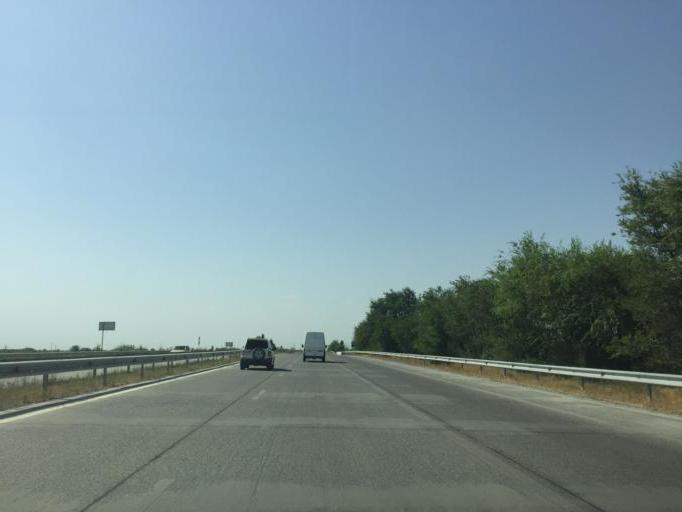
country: AM
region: Ararat
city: Burastan
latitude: 39.9763
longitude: 44.4978
